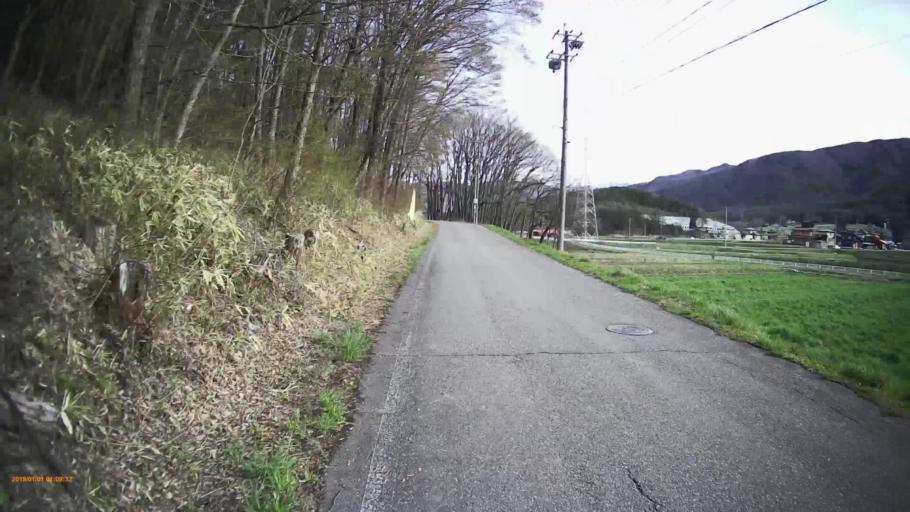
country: JP
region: Nagano
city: Chino
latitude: 35.9149
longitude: 138.2200
